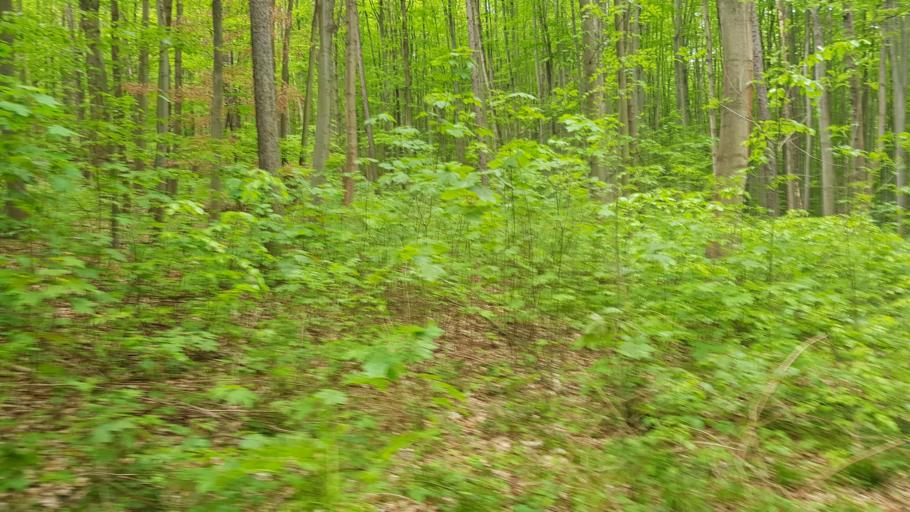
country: DE
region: Saxony-Anhalt
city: Neinstedt
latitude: 51.7405
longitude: 11.0674
